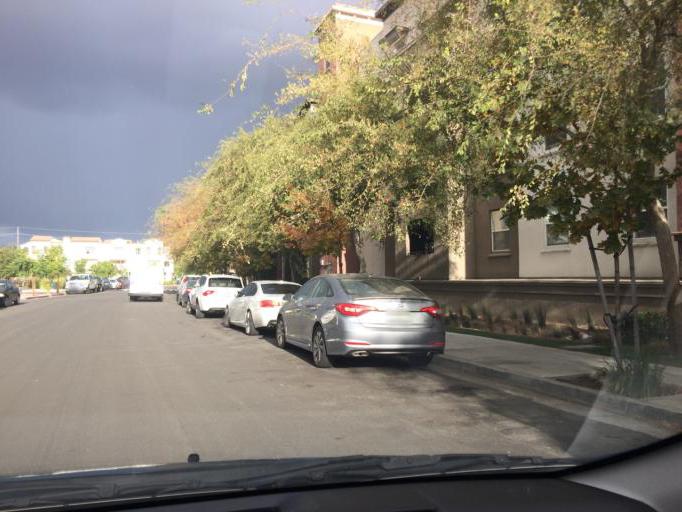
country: US
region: California
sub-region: Santa Clara County
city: Seven Trees
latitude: 37.2914
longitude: -121.8527
